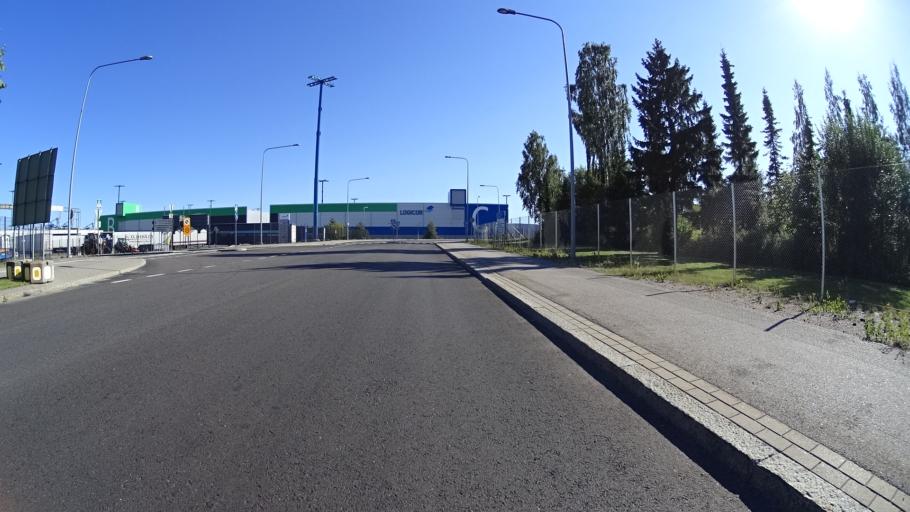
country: FI
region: Uusimaa
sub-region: Helsinki
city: Vantaa
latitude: 60.2201
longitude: 25.1740
